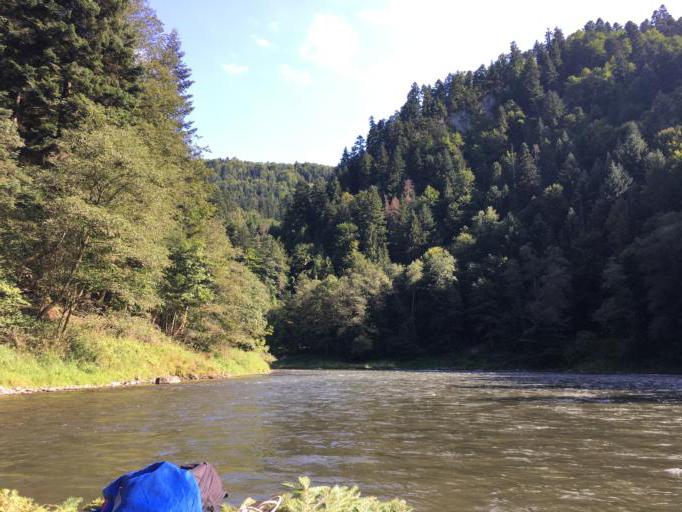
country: PL
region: Lesser Poland Voivodeship
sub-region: Powiat nowotarski
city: Kroscienko nad Dunajcem
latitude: 49.3968
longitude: 20.4306
